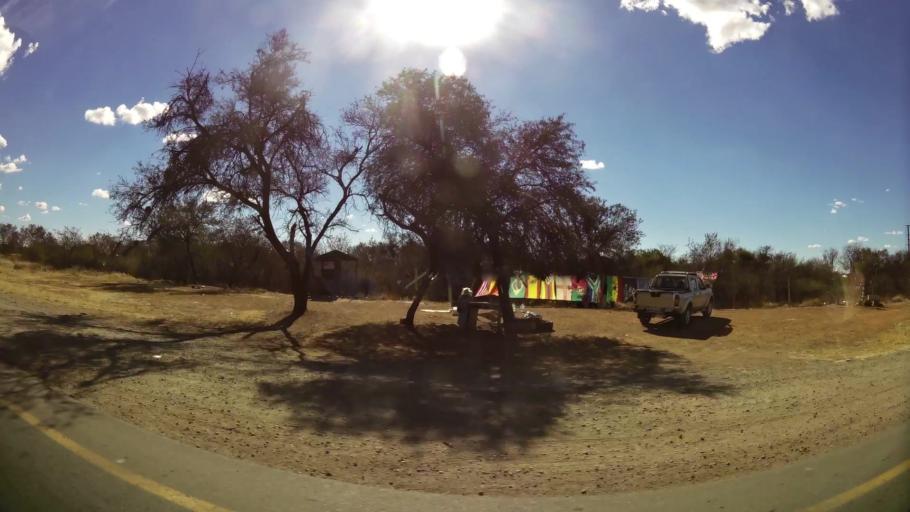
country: ZA
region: North-West
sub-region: Dr Kenneth Kaunda District Municipality
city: Klerksdorp
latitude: -26.8687
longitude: 26.6255
